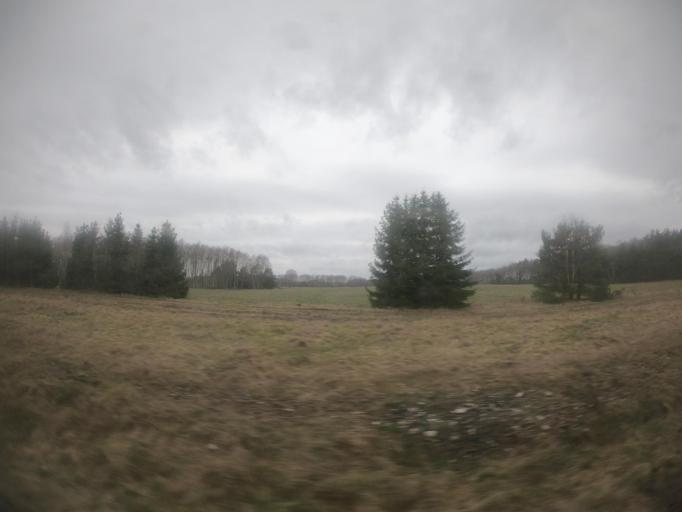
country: PL
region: West Pomeranian Voivodeship
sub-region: Powiat szczecinecki
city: Bialy Bor
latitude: 53.8135
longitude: 16.8679
